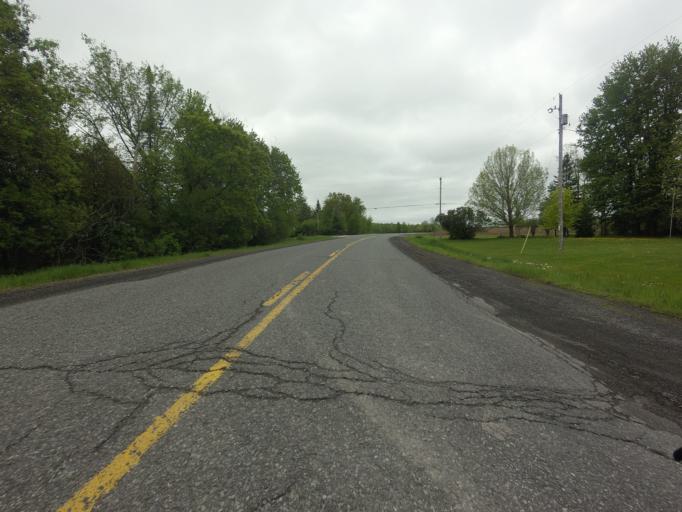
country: US
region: New York
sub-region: St. Lawrence County
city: Norfolk
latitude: 44.9830
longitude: -75.1555
